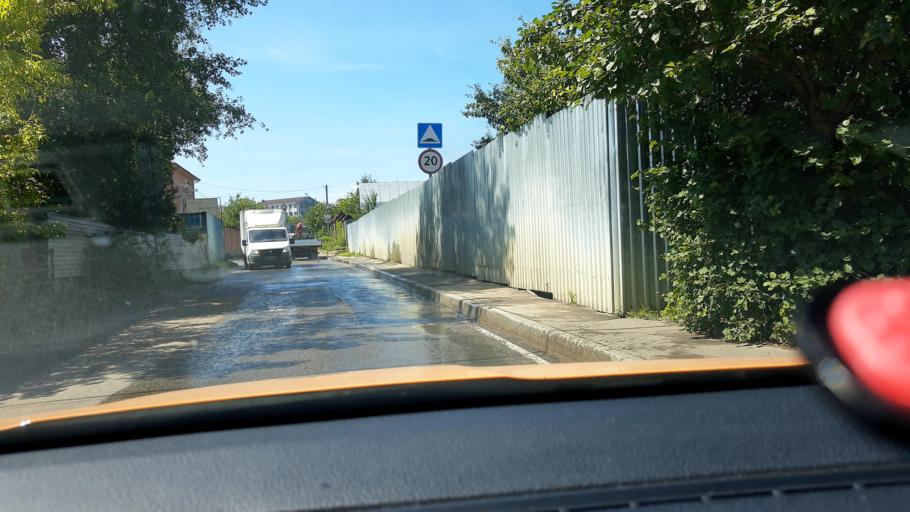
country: RU
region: Moscow
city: Severnyy
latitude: 55.9477
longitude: 37.5321
